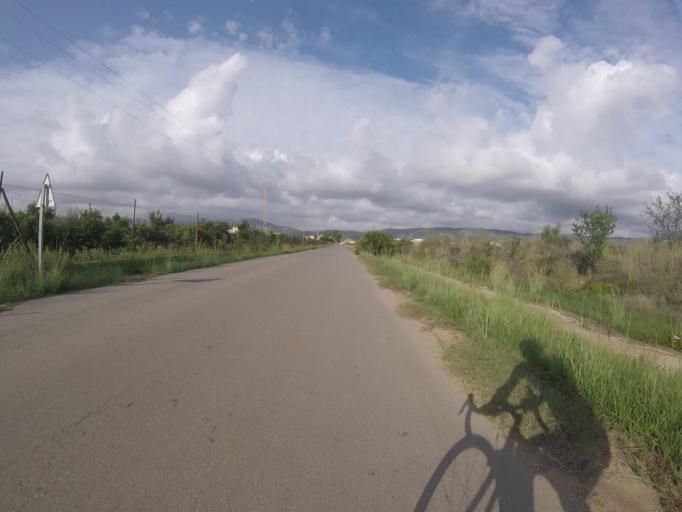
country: ES
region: Valencia
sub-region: Provincia de Castello
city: Orpesa/Oropesa del Mar
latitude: 40.1387
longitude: 0.1554
